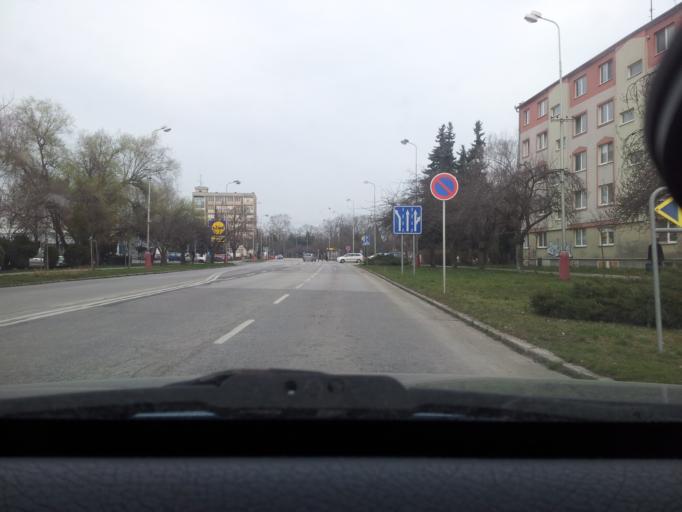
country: SK
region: Nitriansky
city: Levice
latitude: 48.2132
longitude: 18.5977
